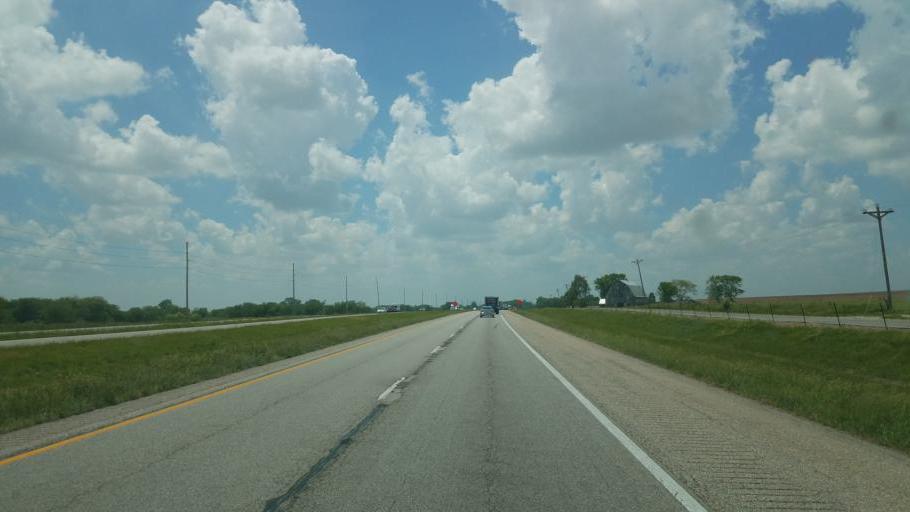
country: US
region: Illinois
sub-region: Madison County
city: Highland
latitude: 38.8101
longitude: -89.5792
